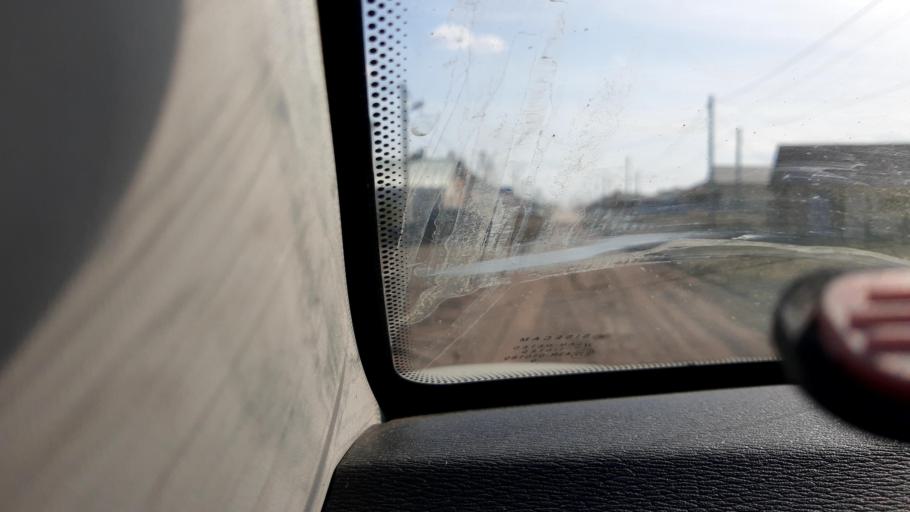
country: RU
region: Bashkortostan
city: Kabakovo
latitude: 54.6175
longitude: 56.0925
